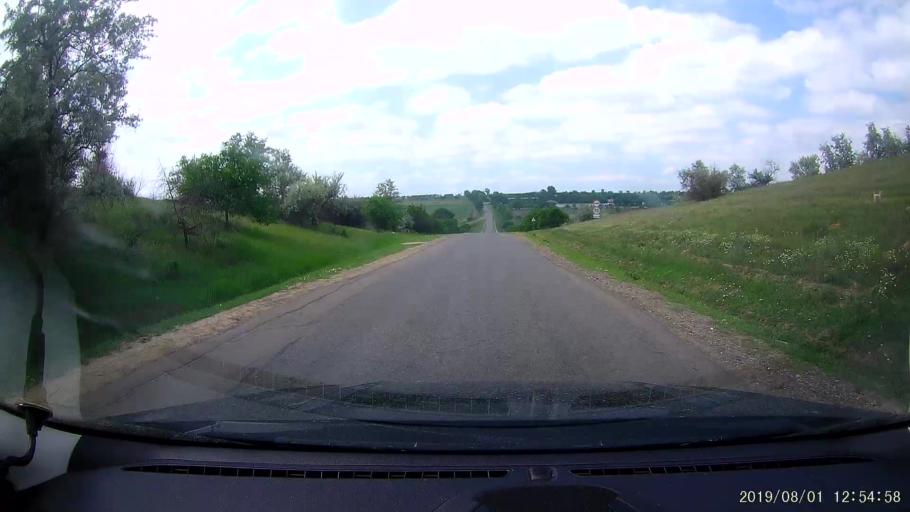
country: MD
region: Gagauzia
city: Vulcanesti
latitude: 45.6944
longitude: 28.4763
